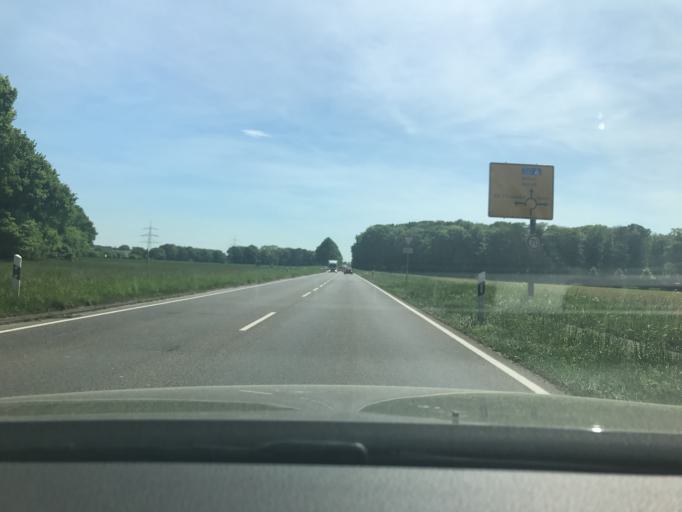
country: DE
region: North Rhine-Westphalia
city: Tonisvorst
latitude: 51.3034
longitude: 6.4777
